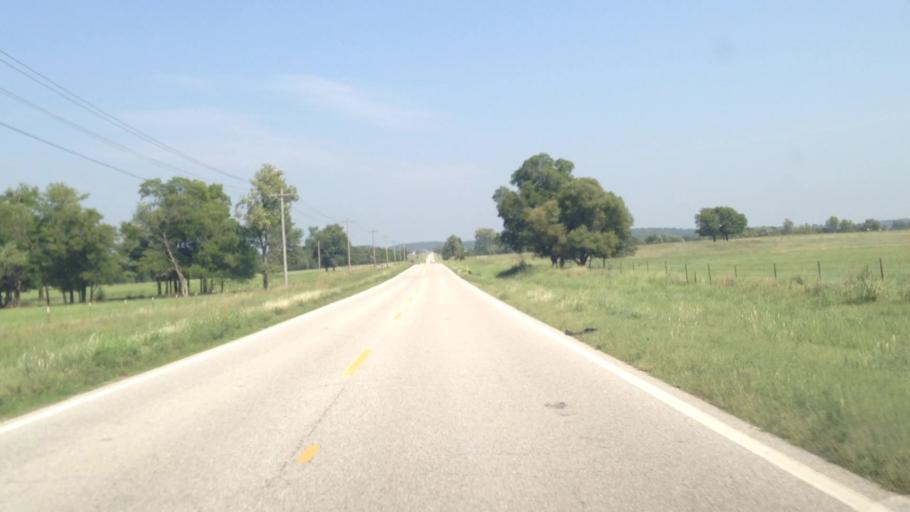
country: US
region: Oklahoma
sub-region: Craig County
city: Vinita
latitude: 36.7442
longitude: -95.1436
